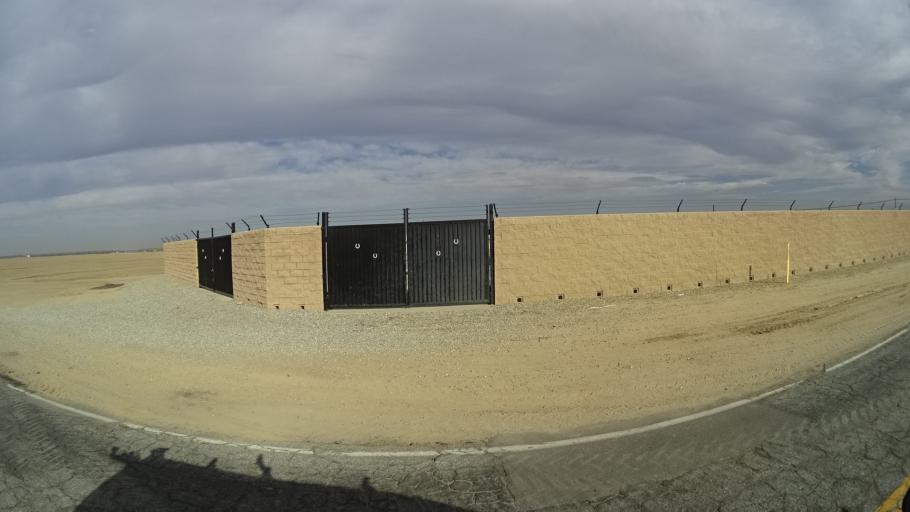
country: US
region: California
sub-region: Kern County
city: Rosedale
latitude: 35.4125
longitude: -119.1647
